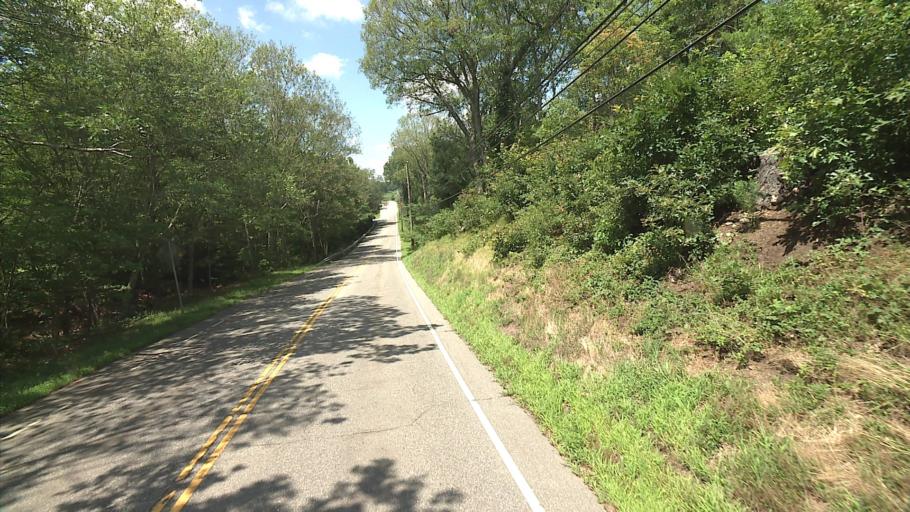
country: US
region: Connecticut
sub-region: Windham County
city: Windham
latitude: 41.6998
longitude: -72.1399
